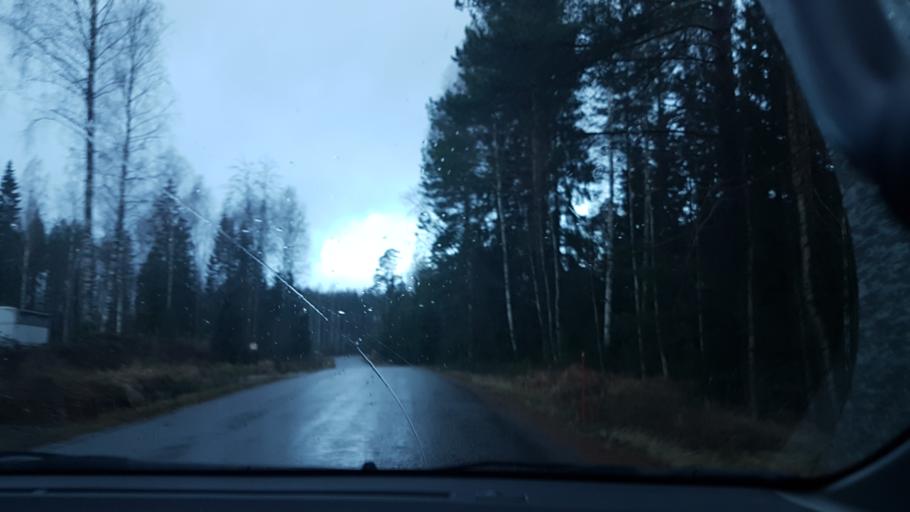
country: FI
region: Uusimaa
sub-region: Helsinki
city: Lohja
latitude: 60.2157
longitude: 24.0916
